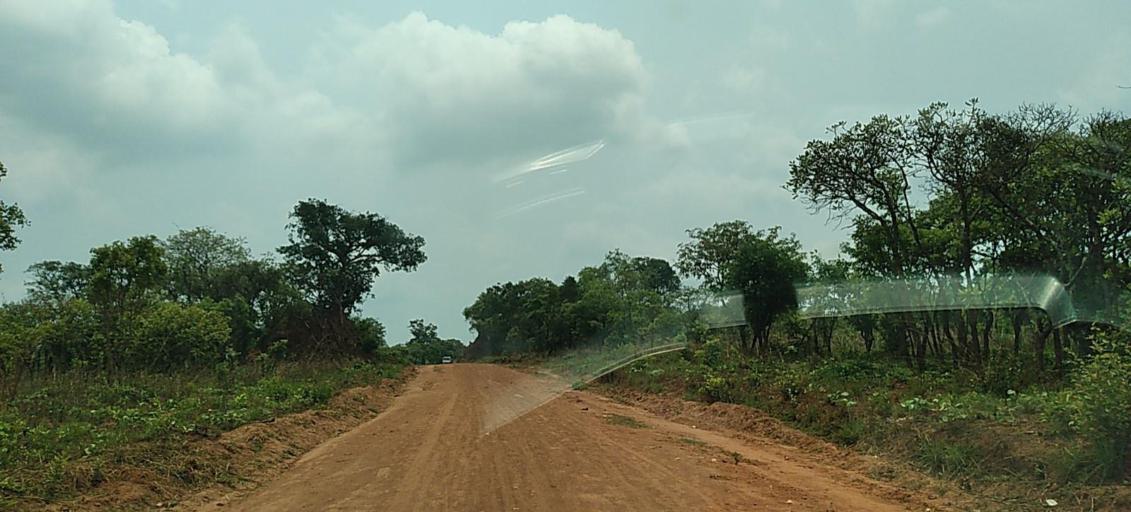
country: ZM
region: North-Western
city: Mwinilunga
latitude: -11.4561
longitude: 24.7589
